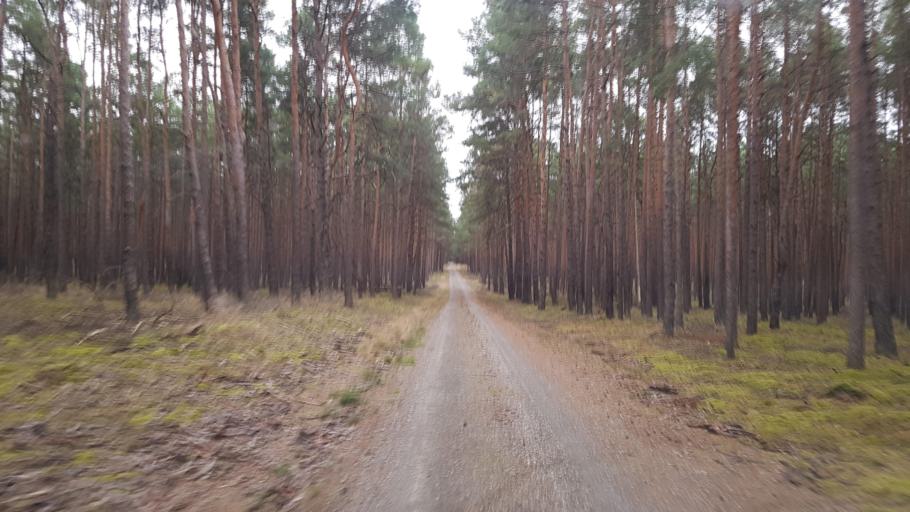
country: DE
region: Brandenburg
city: Sonnewalde
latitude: 51.7456
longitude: 13.6530
